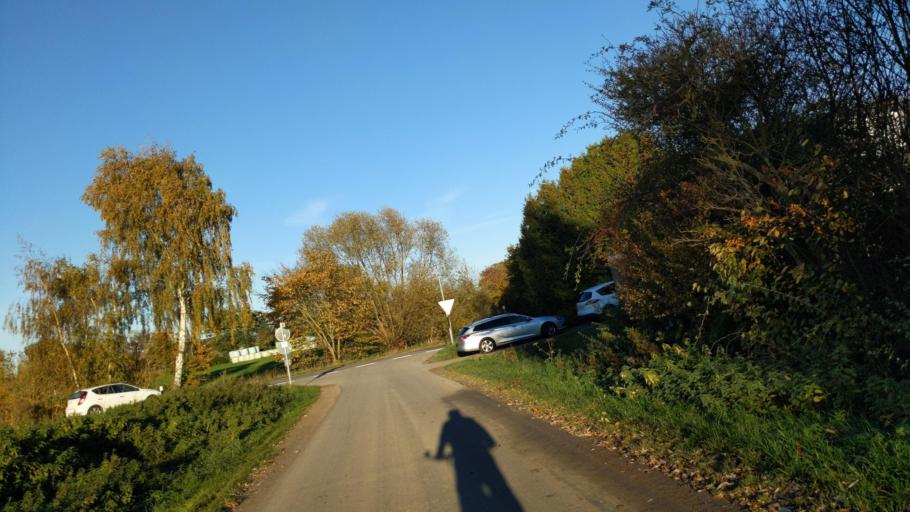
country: DE
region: Schleswig-Holstein
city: Gross Sarau
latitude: 53.7687
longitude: 10.7313
